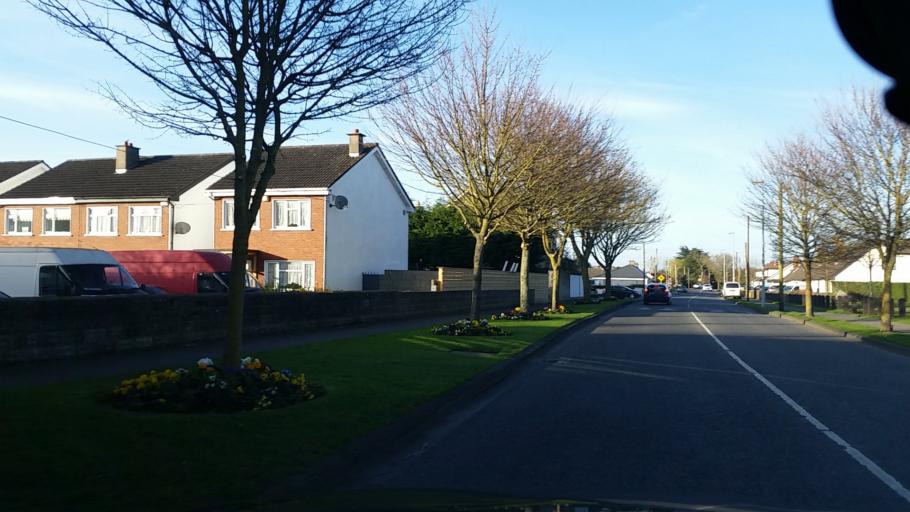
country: IE
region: Leinster
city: Hartstown
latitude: 53.3925
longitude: -6.4083
